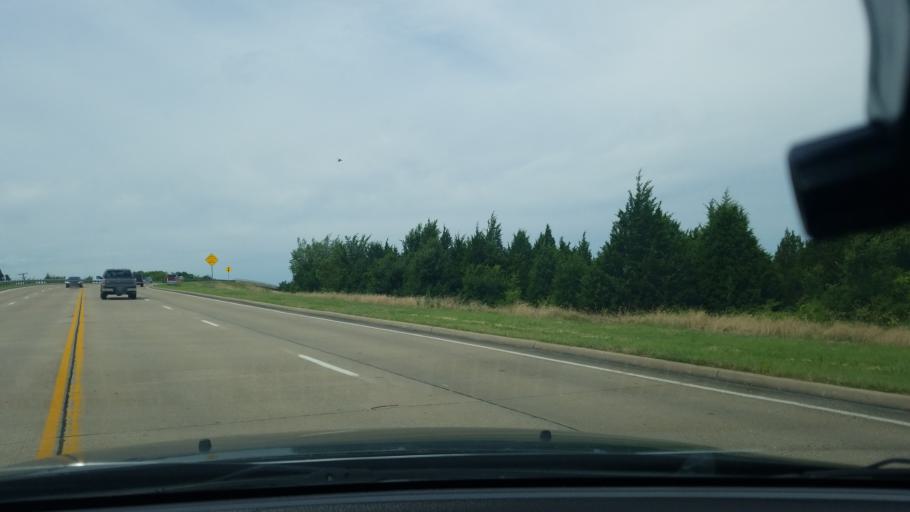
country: US
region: Texas
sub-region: Dallas County
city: Mesquite
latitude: 32.7672
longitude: -96.5781
